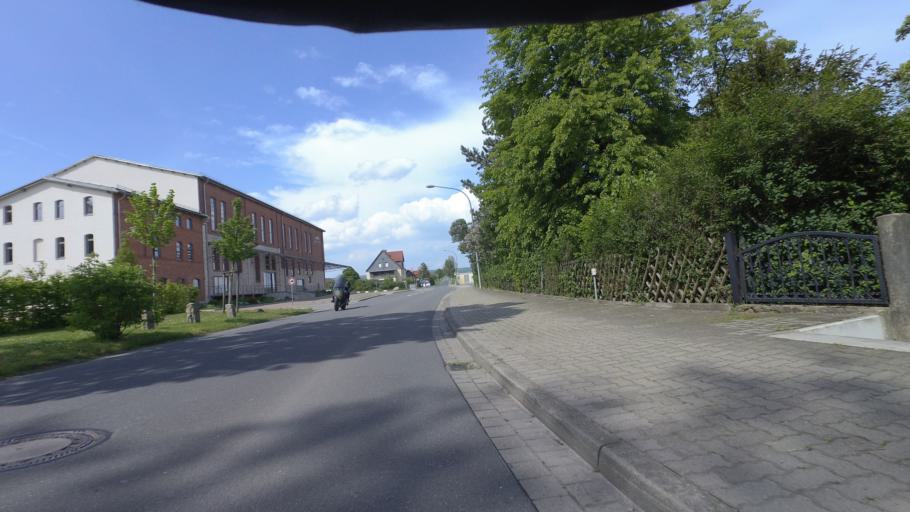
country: DE
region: Lower Saxony
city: Sollingen
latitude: 52.0961
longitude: 10.9258
